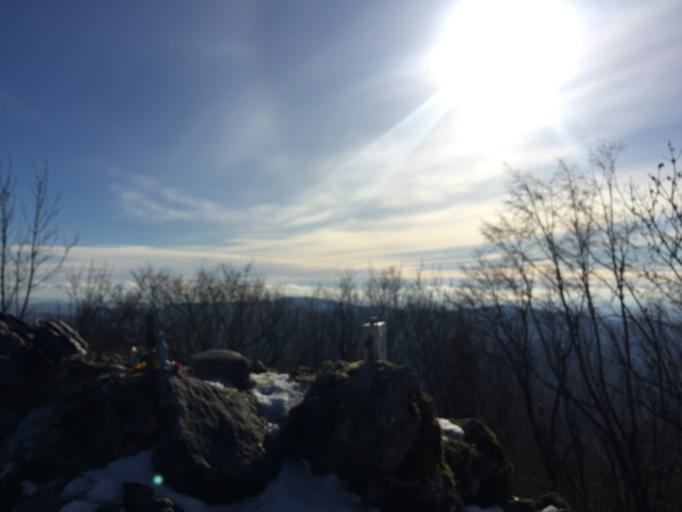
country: IT
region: Friuli Venezia Giulia
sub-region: Provincia di Udine
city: Clodig
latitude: 46.1717
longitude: 13.5865
